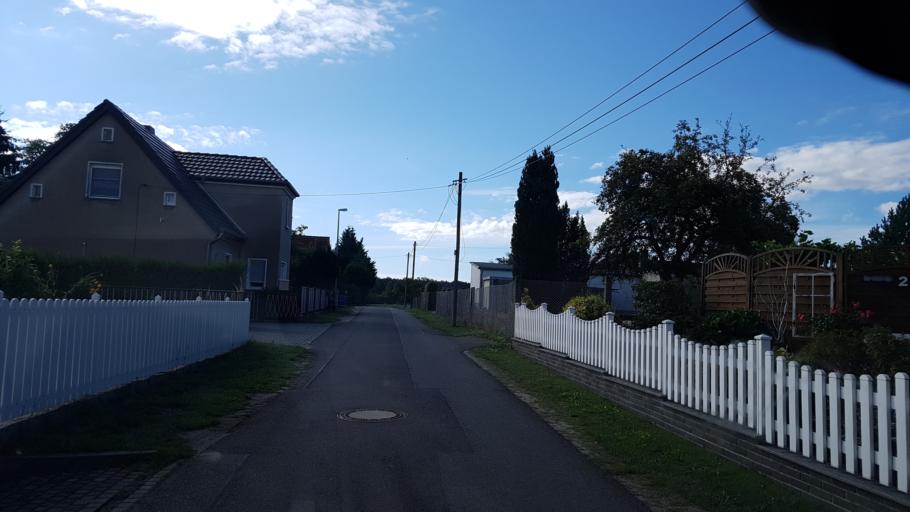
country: DE
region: Brandenburg
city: Tschernitz
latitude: 51.6375
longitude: 14.5955
